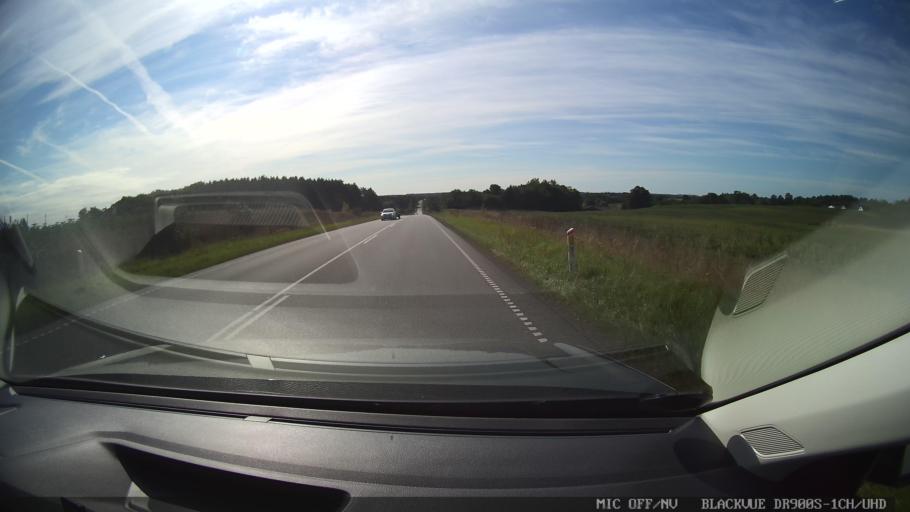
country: DK
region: North Denmark
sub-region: Mariagerfjord Kommune
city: Hadsund
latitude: 56.7628
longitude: 10.0660
